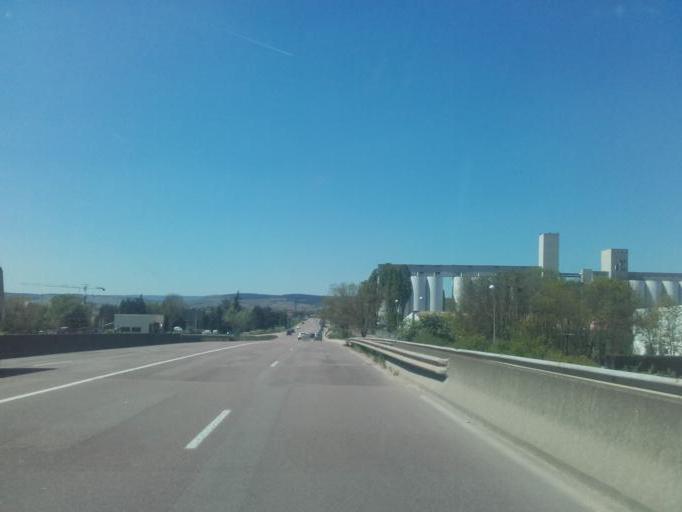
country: FR
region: Bourgogne
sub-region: Departement de la Cote-d'Or
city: Beaune
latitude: 47.0177
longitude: 4.8685
